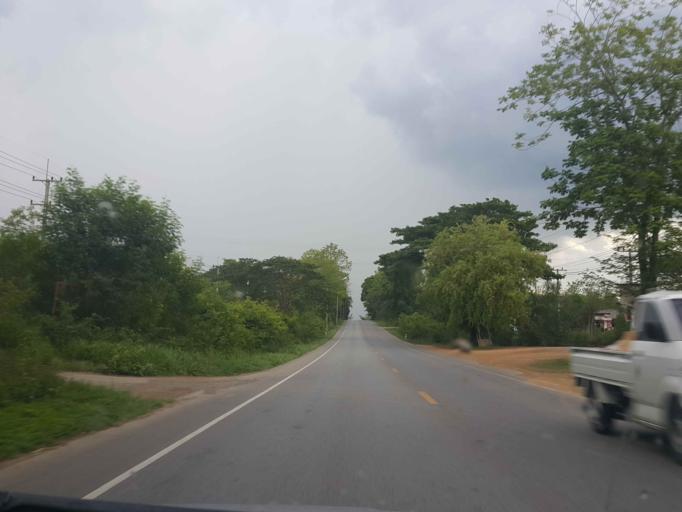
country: TH
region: Phrae
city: Den Chai
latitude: 17.9710
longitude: 100.0454
